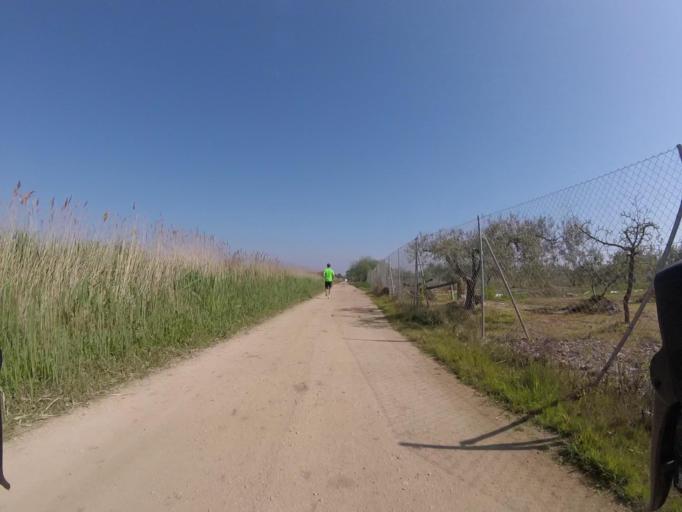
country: ES
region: Valencia
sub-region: Provincia de Castello
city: Orpesa/Oropesa del Mar
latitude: 40.1435
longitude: 0.1642
